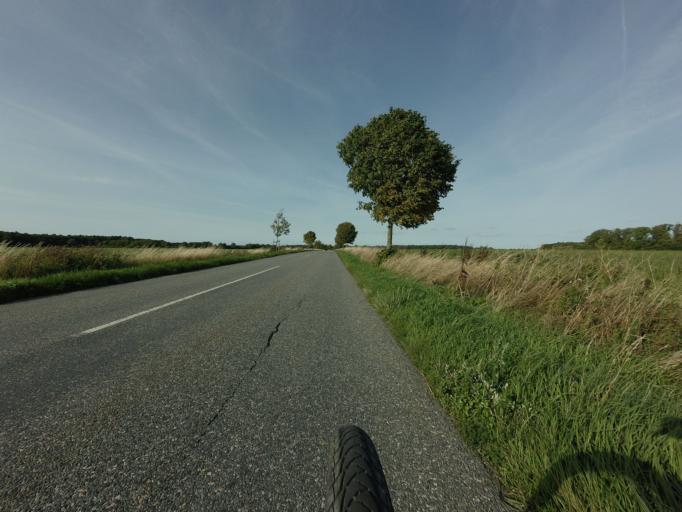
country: DK
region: Zealand
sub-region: Faxe Kommune
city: Fakse Ladeplads
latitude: 55.2436
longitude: 12.2183
